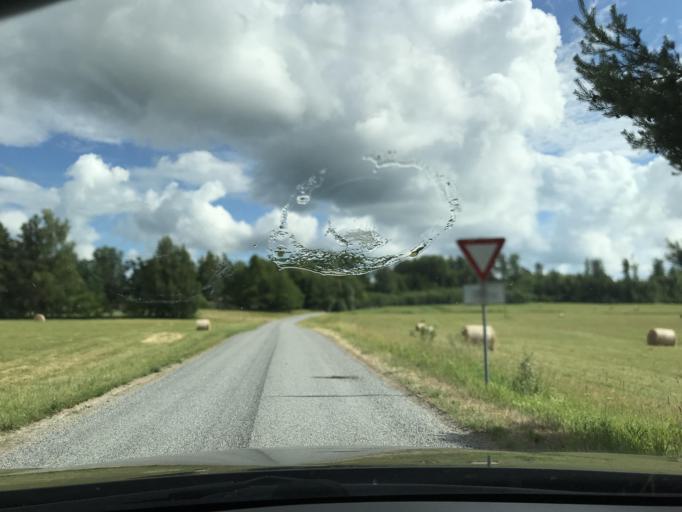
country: LV
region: Alsunga
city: Alsunga
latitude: 56.9758
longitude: 21.6399
